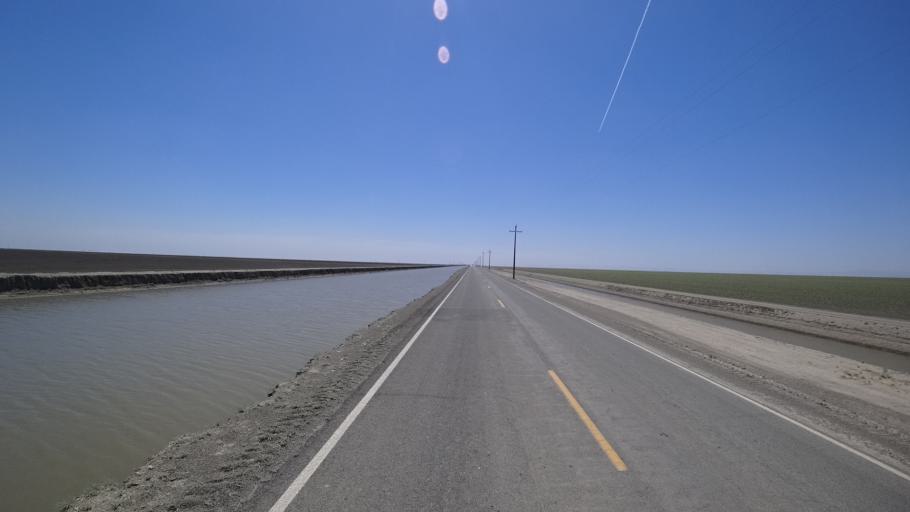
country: US
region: California
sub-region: Kings County
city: Corcoran
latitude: 36.0347
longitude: -119.6433
